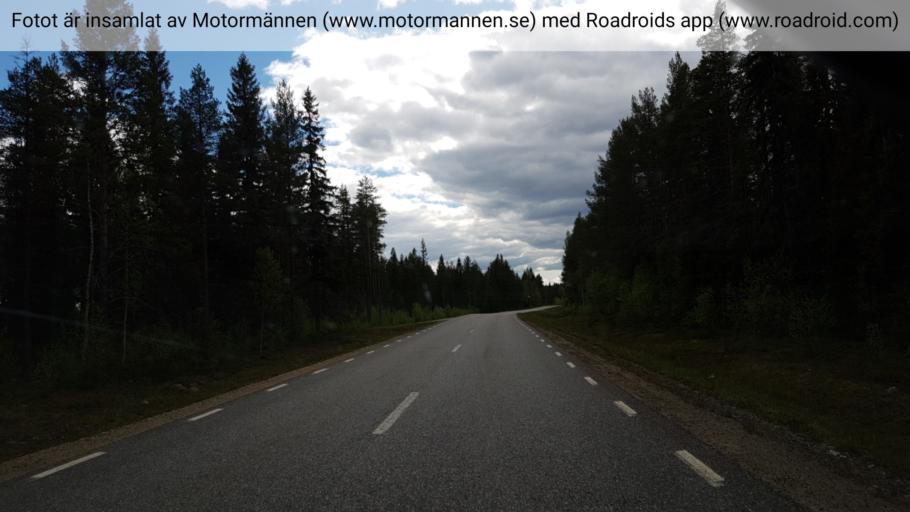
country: SE
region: Vaesterbotten
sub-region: Skelleftea Kommun
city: Langsele
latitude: 64.6361
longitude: 19.9859
